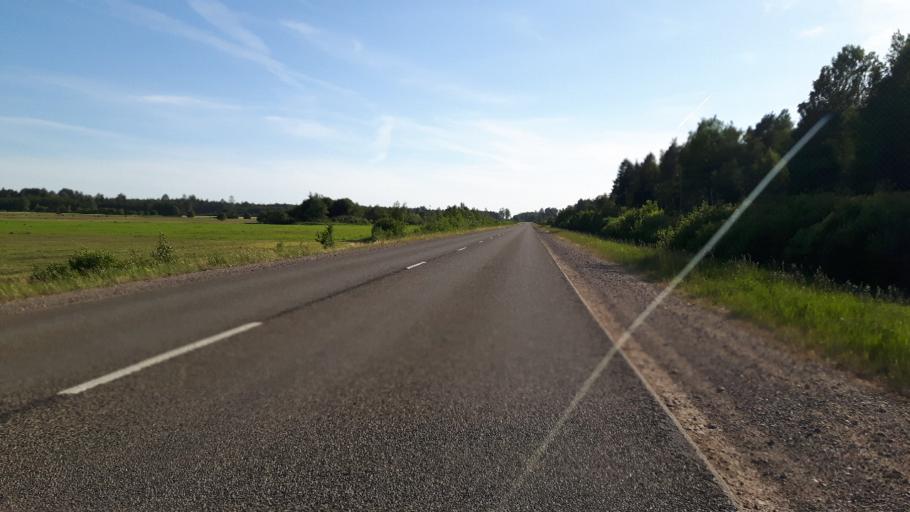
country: LV
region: Talsu Rajons
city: Stende
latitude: 57.0618
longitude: 22.2781
